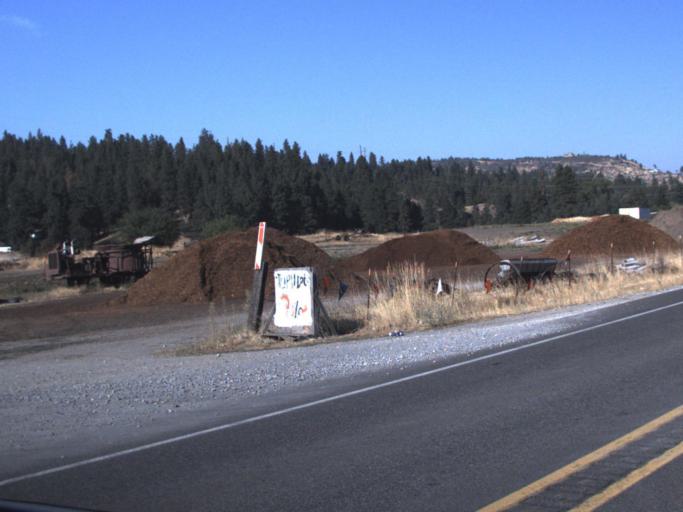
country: US
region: Washington
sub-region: Spokane County
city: Liberty Lake
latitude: 47.7072
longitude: -117.1213
